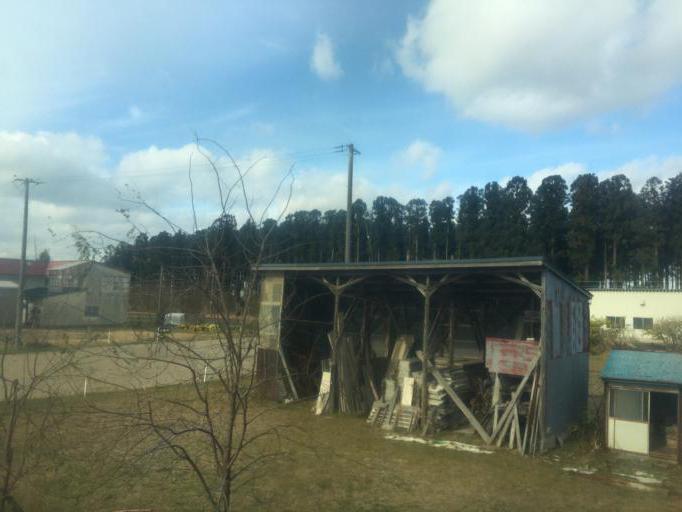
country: JP
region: Akita
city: Noshiromachi
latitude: 40.1891
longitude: 140.0603
